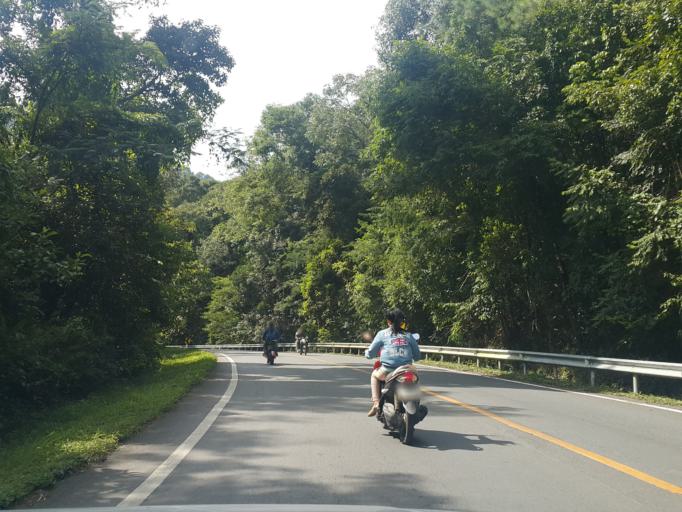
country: TH
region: Chiang Mai
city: Mae Chaem
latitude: 18.5494
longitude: 98.5413
